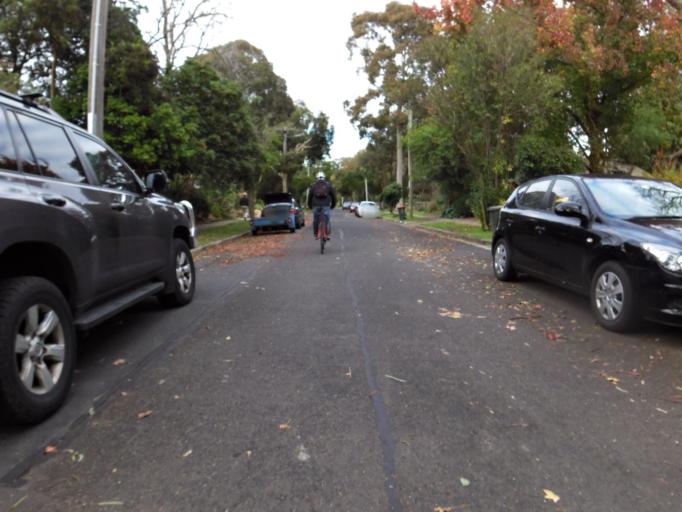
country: AU
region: Victoria
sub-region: Whitehorse
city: Nunawading
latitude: -37.8220
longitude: 145.1641
